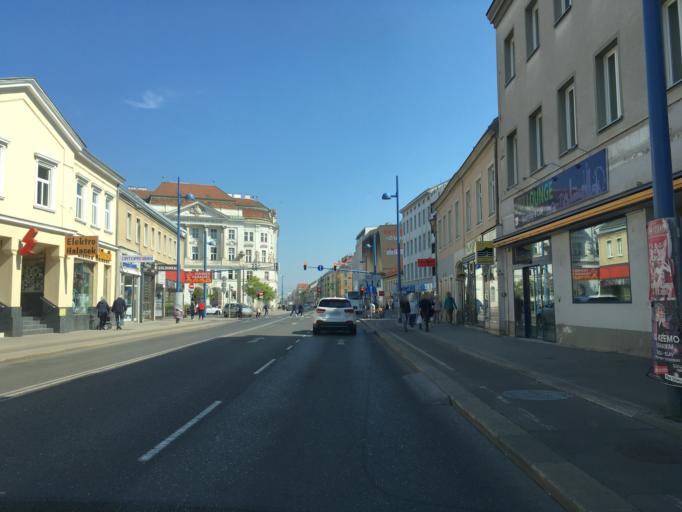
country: AT
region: Vienna
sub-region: Wien Stadt
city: Vienna
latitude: 48.2566
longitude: 16.3970
